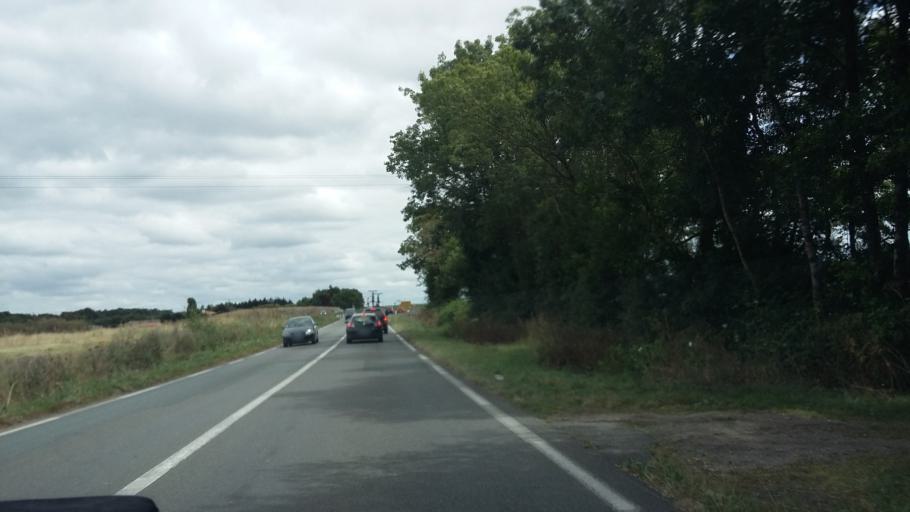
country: FR
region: Pays de la Loire
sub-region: Departement de la Vendee
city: Challans
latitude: 46.8360
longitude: -1.8374
